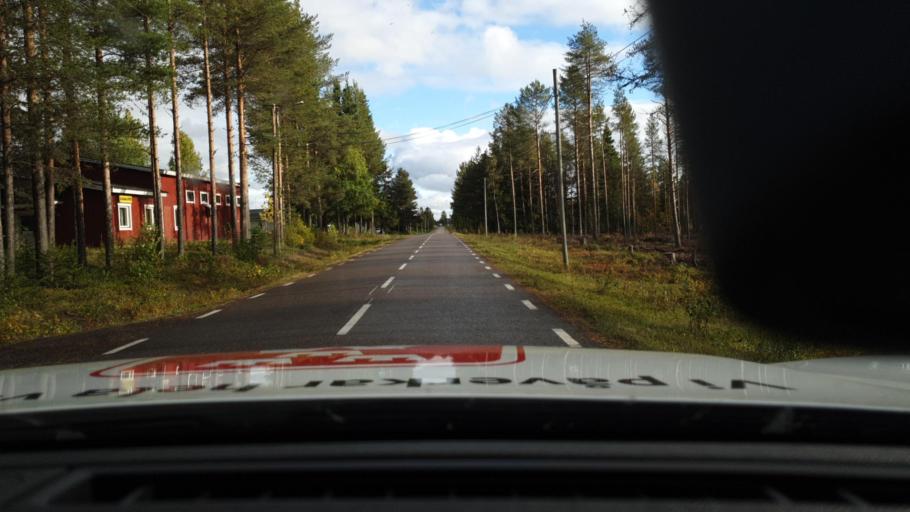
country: SE
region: Norrbotten
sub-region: Overkalix Kommun
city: OEverkalix
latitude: 67.0078
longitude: 22.4861
